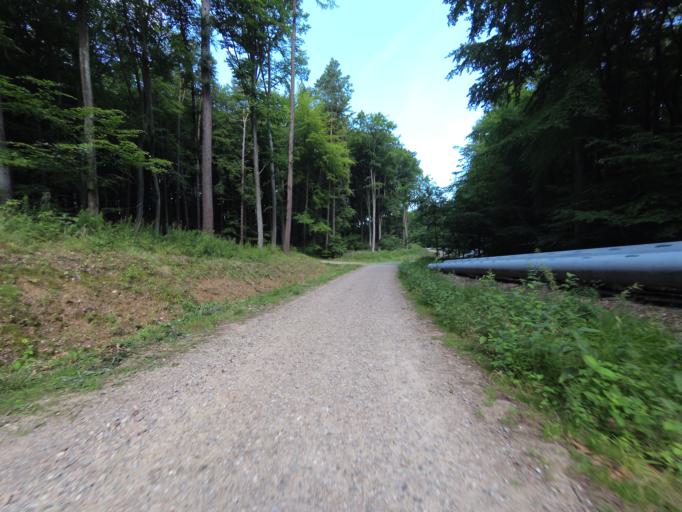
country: PL
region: Pomeranian Voivodeship
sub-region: Gdynia
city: Wielki Kack
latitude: 54.4793
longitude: 18.5007
